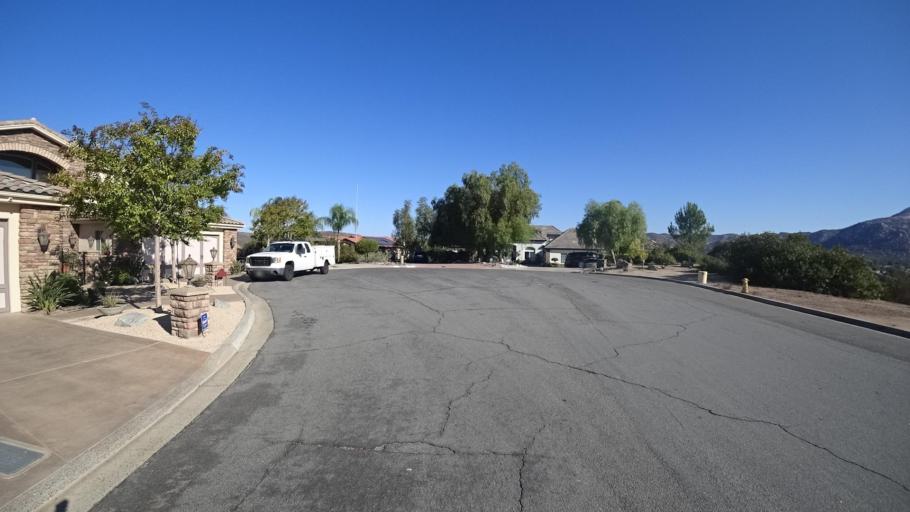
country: US
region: California
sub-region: San Diego County
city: San Diego Country Estates
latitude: 32.9953
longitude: -116.8069
